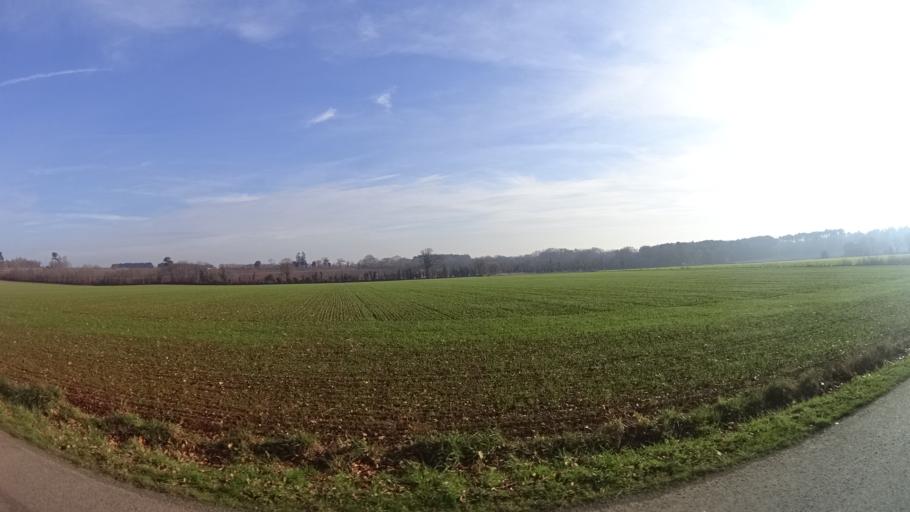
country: FR
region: Brittany
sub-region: Departement du Morbihan
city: Allaire
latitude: 47.6100
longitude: -2.1470
